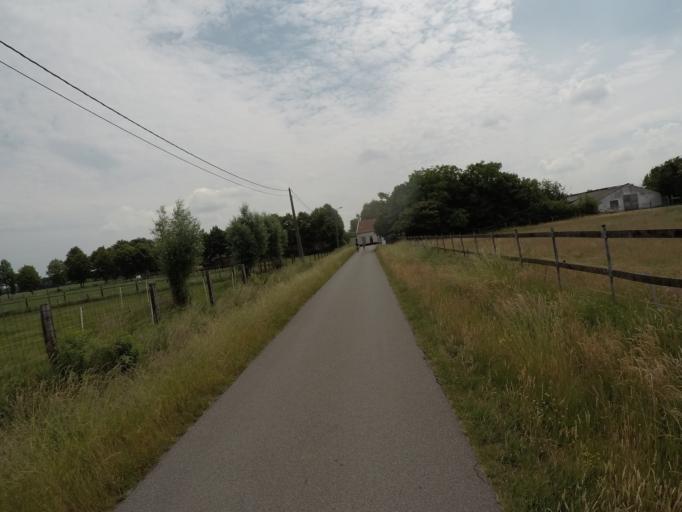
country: BE
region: Flanders
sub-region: Provincie Antwerpen
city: Essen
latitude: 51.4321
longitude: 4.5317
